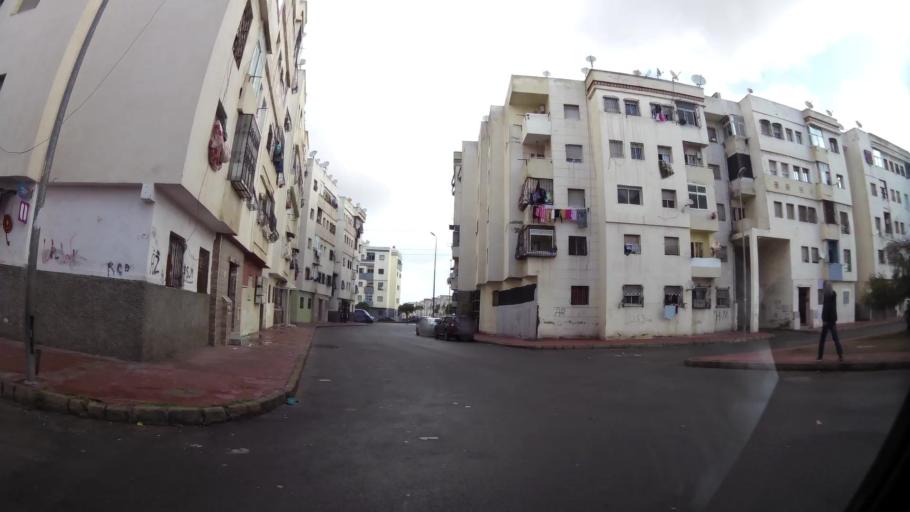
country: MA
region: Grand Casablanca
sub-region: Mediouna
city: Tit Mellil
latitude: 33.5917
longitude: -7.5382
